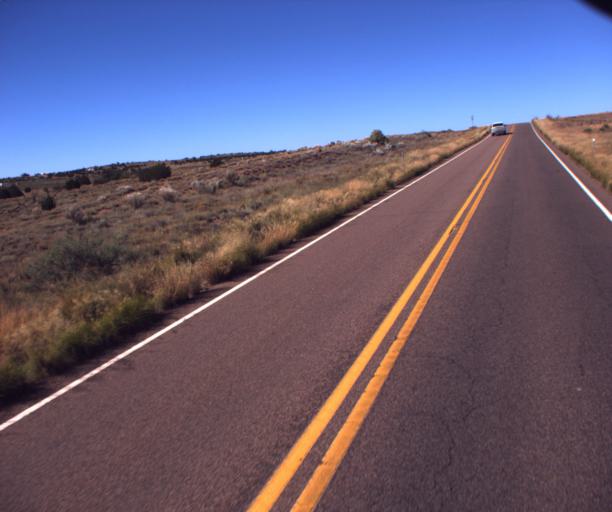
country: US
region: Arizona
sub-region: Navajo County
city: Snowflake
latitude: 34.5129
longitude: -110.1424
